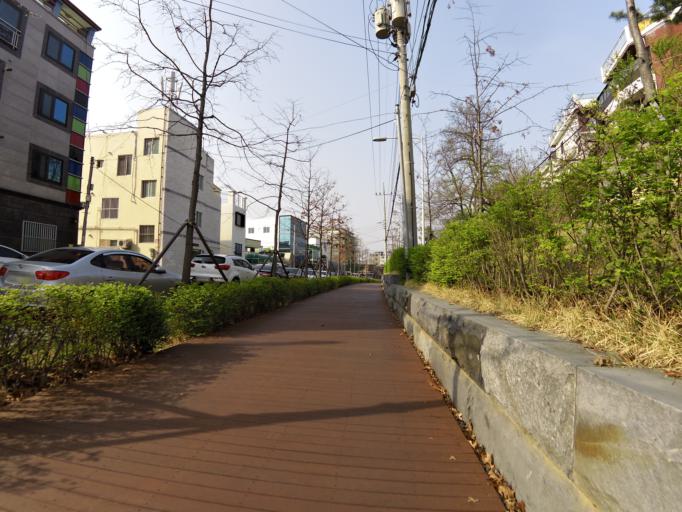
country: KR
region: Daegu
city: Daegu
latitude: 35.8873
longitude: 128.6364
